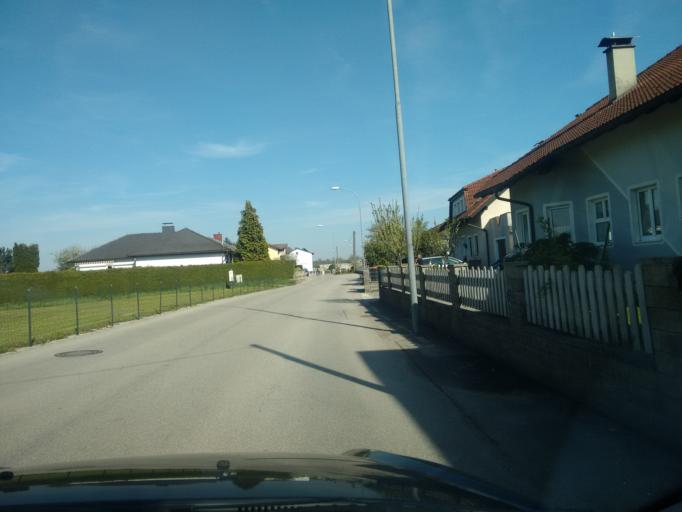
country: AT
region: Upper Austria
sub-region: Wels-Land
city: Holzhausen
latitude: 48.1963
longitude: 14.0794
